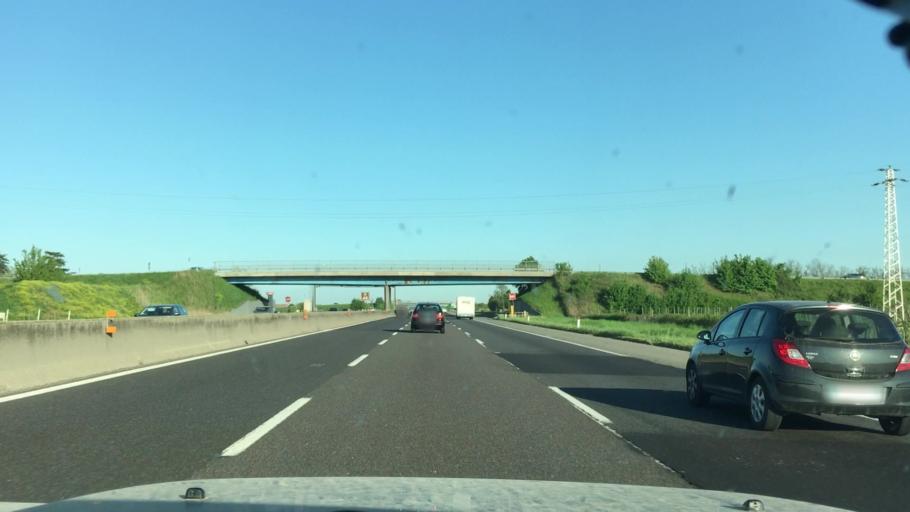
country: IT
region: Emilia-Romagna
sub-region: Provincia di Bologna
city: Imola
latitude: 44.3766
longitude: 11.7535
